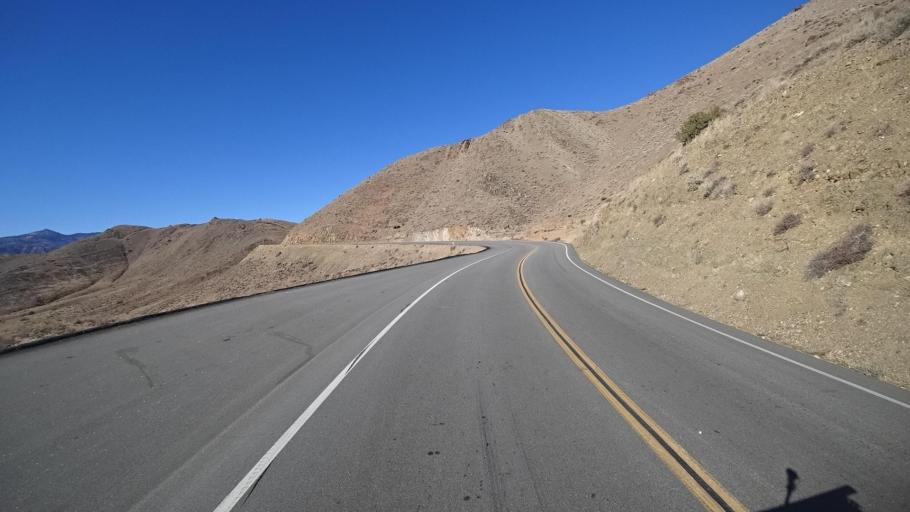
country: US
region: California
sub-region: Kern County
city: Wofford Heights
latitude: 35.6837
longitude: -118.4248
